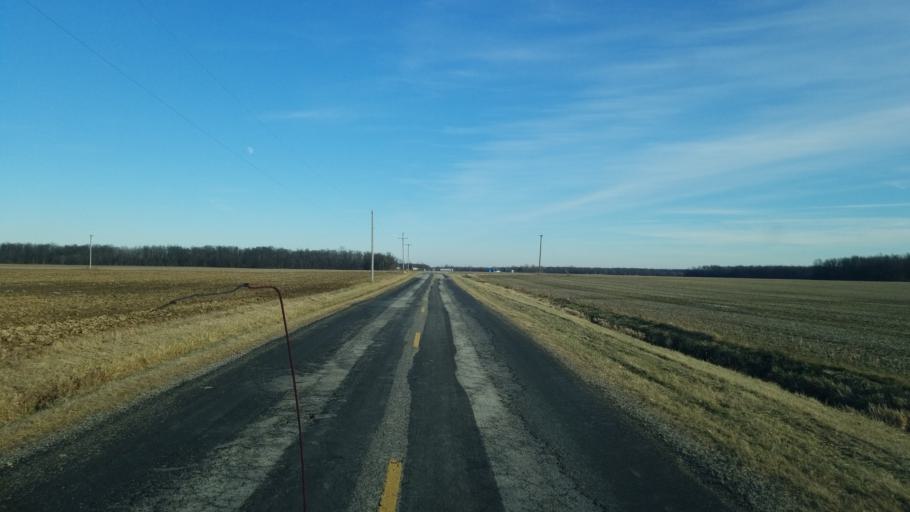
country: US
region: Ohio
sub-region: Huron County
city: Bellevue
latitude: 41.1799
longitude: -82.8091
